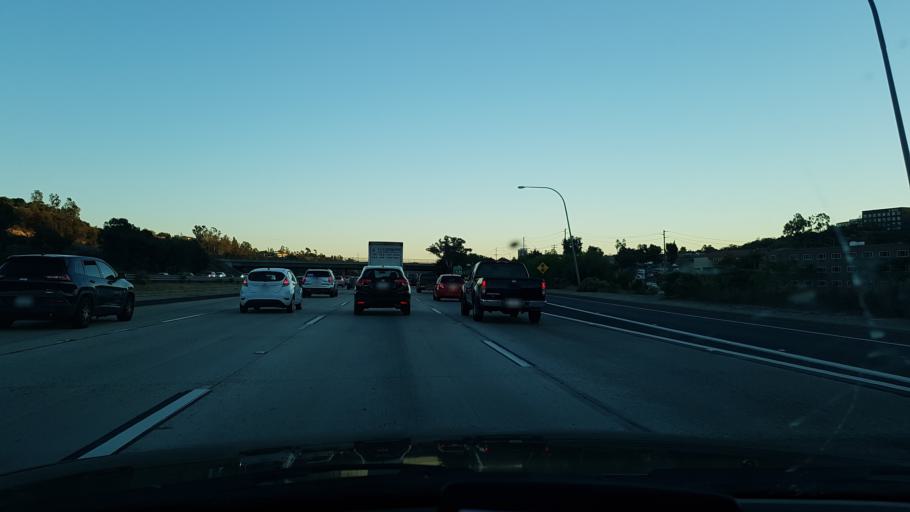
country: US
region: California
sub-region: San Diego County
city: La Mesa
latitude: 32.8136
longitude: -117.1148
